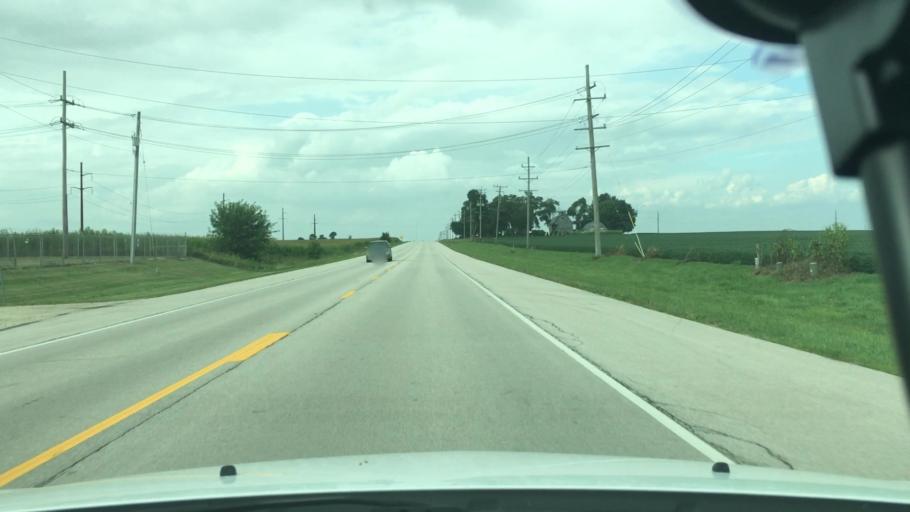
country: US
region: Illinois
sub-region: DeKalb County
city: Waterman
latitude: 41.8277
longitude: -88.7539
